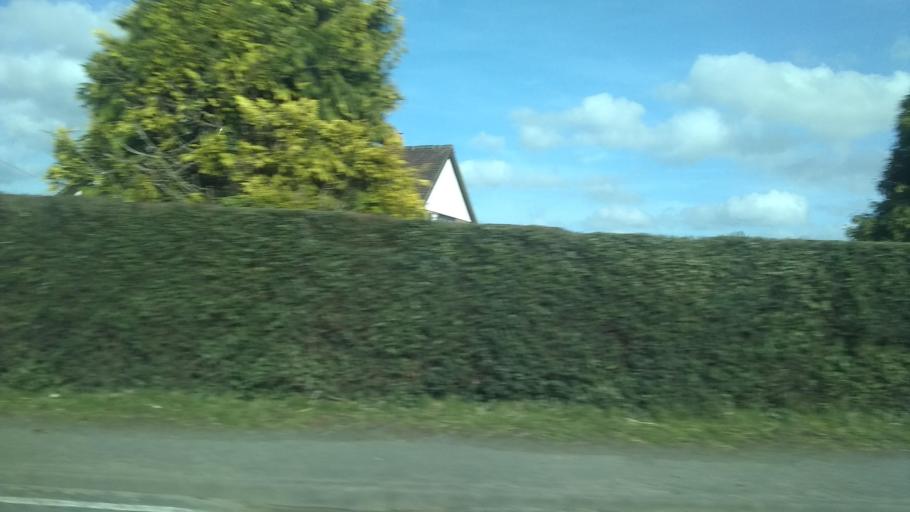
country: GB
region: England
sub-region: Worcestershire
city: Bewdley
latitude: 52.3656
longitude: -2.3947
